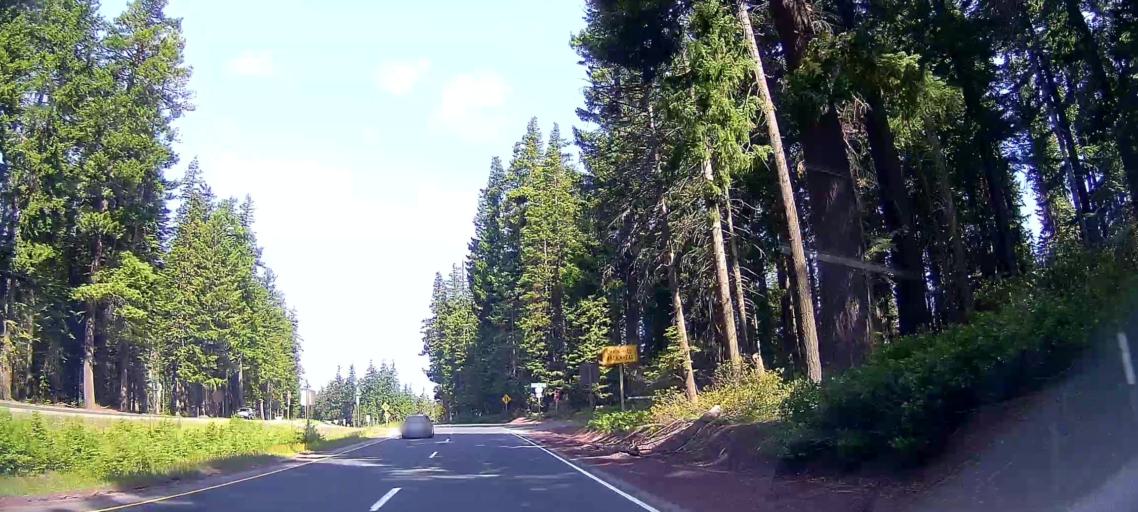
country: US
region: Oregon
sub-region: Clackamas County
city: Mount Hood Village
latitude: 45.1299
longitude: -121.5988
